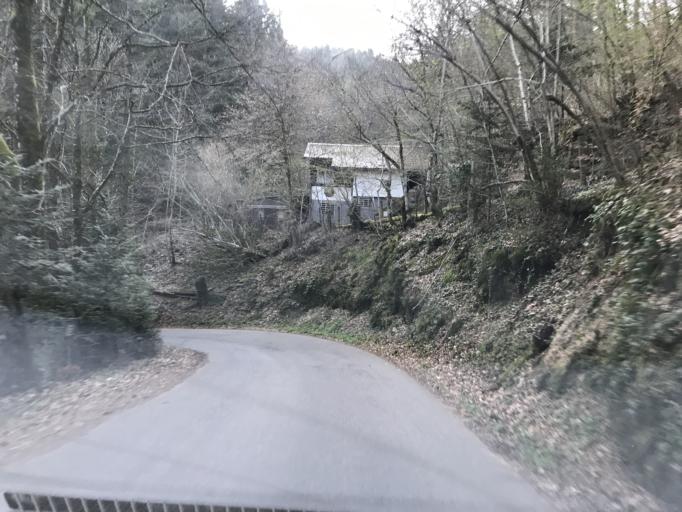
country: DE
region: Baden-Wuerttemberg
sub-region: Freiburg Region
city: Hausen
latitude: 47.6848
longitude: 7.8321
